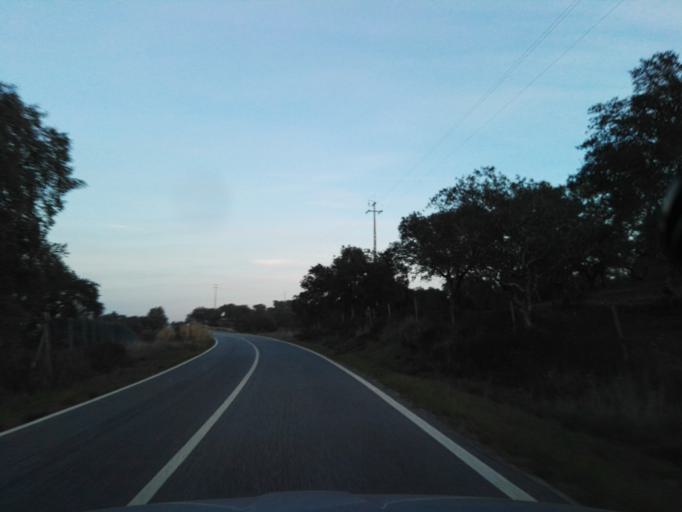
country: PT
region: Evora
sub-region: Montemor-O-Novo
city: Montemor-o-Novo
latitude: 38.7671
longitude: -8.1329
